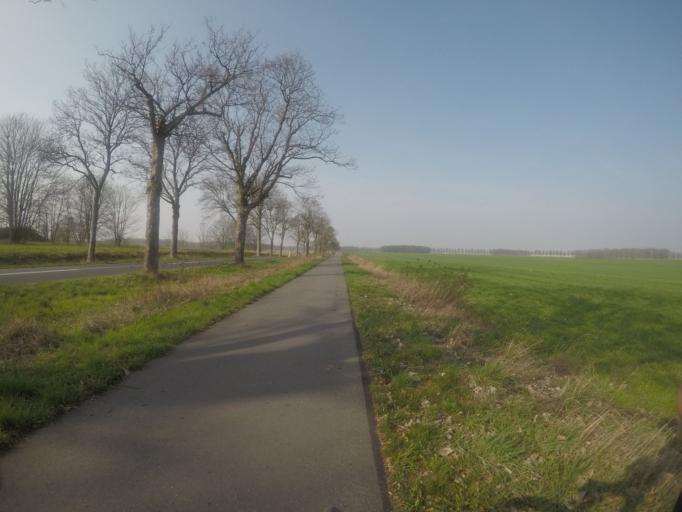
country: DE
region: Brandenburg
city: Mittenwalde
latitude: 52.2938
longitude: 13.5209
